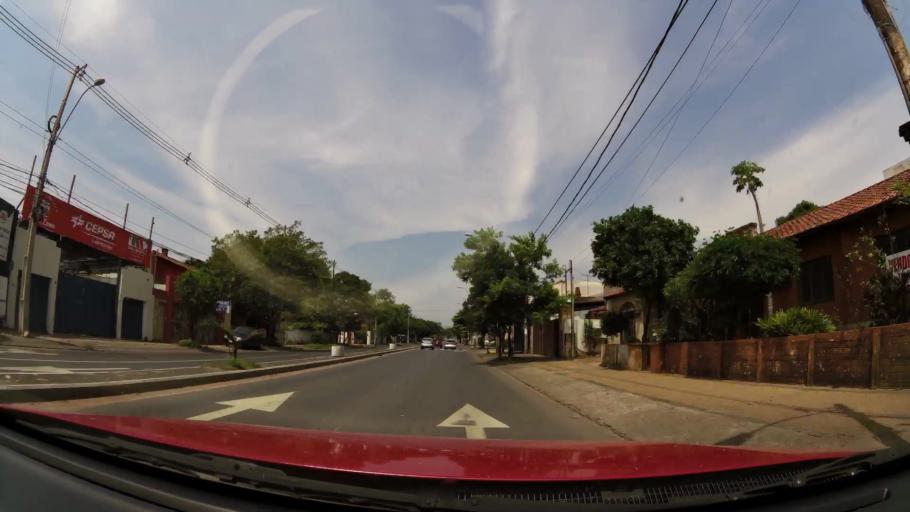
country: PY
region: Asuncion
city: Asuncion
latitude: -25.3043
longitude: -57.5951
